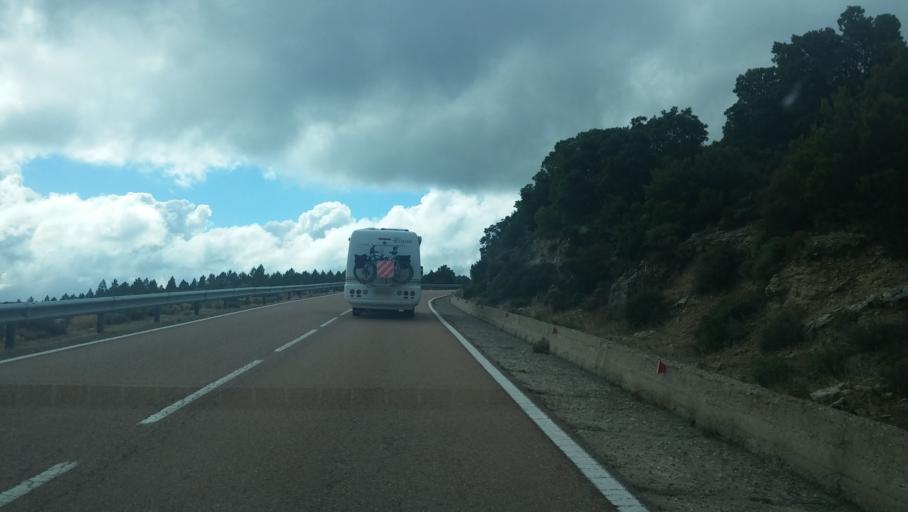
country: IT
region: Sardinia
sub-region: Provincia di Ogliastra
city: Urzulei
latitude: 40.1685
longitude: 9.5274
